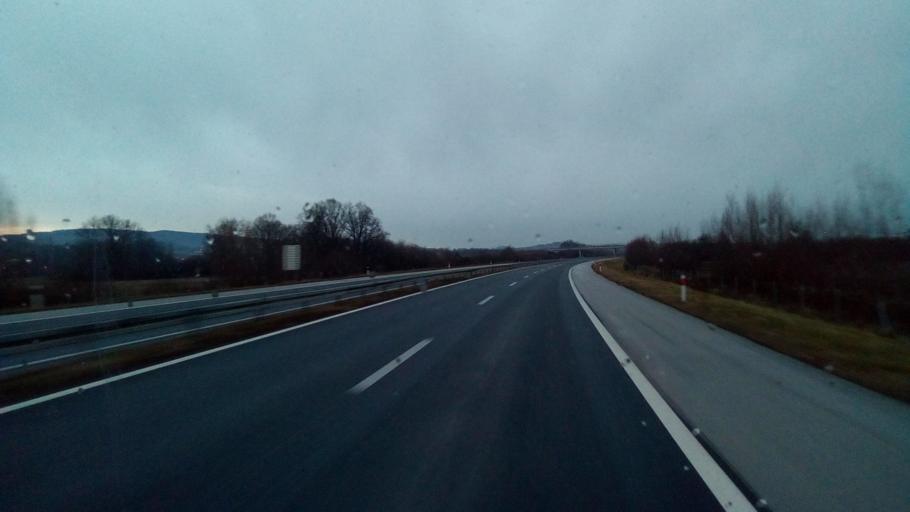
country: HR
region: Zagrebacka
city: Brckovljani
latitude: 45.9374
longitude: 16.2690
